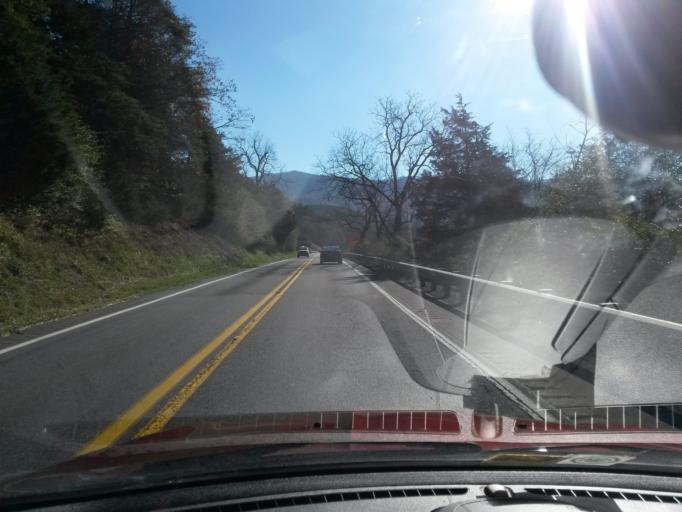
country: US
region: Virginia
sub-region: Alleghany County
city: Clifton Forge
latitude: 37.6800
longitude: -79.8038
